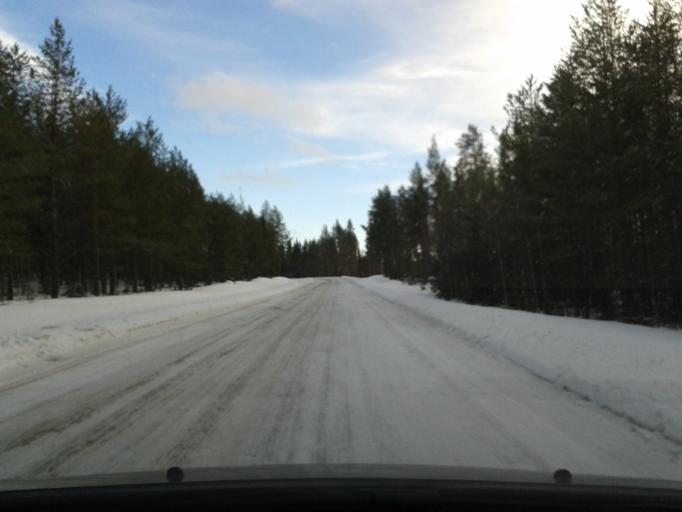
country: SE
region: Vaesterbotten
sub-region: Asele Kommun
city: Asele
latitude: 64.2504
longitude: 17.2758
